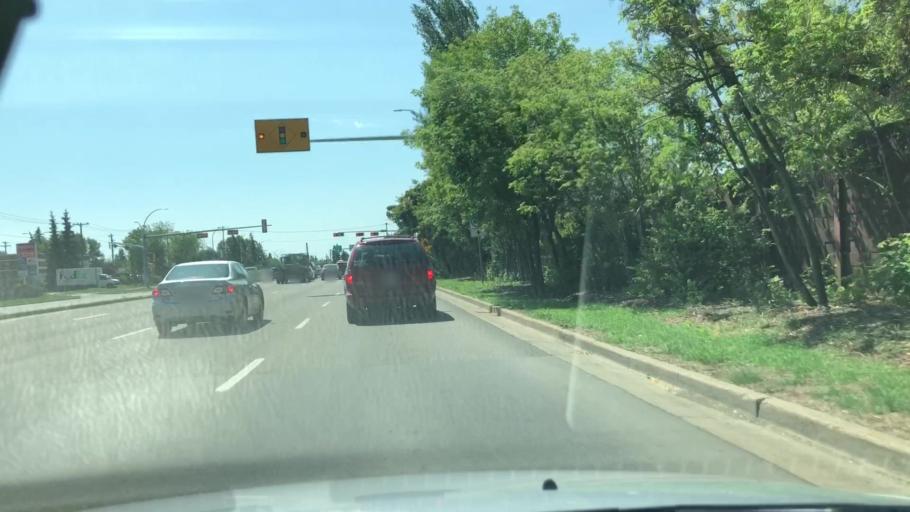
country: CA
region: Alberta
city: Edmonton
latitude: 53.5424
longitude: -113.4439
